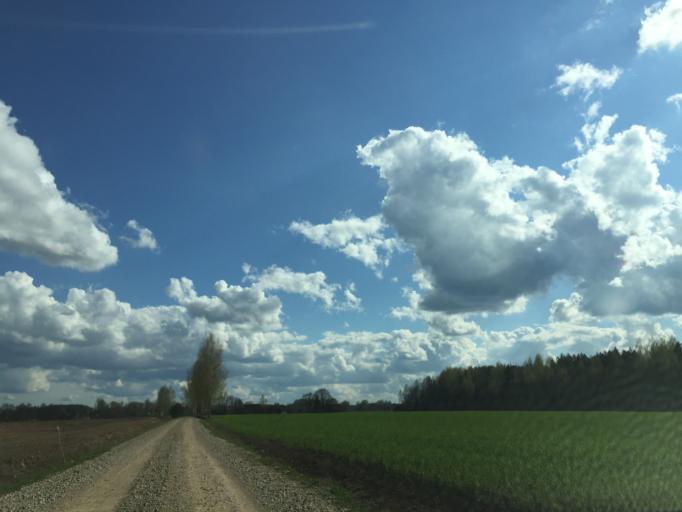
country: LV
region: Beverina
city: Murmuiza
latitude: 57.4256
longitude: 25.5497
